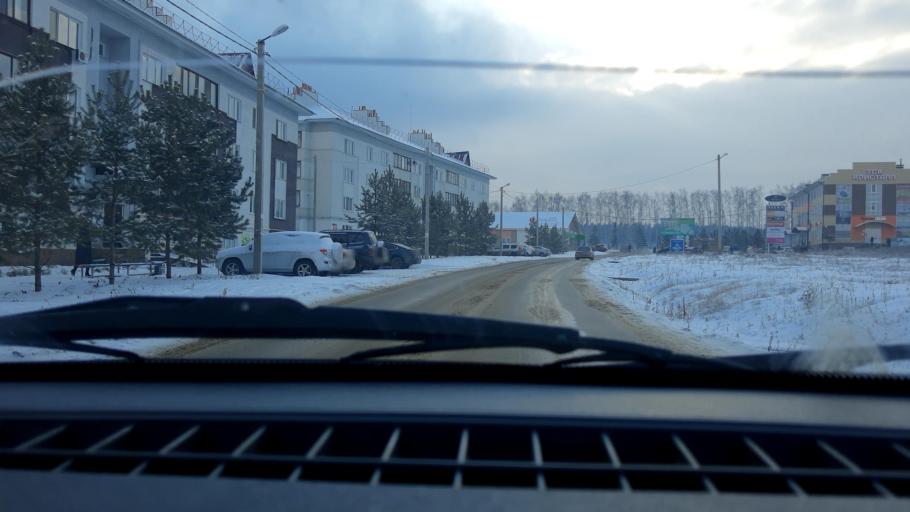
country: RU
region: Bashkortostan
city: Avdon
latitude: 54.4768
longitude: 55.8771
